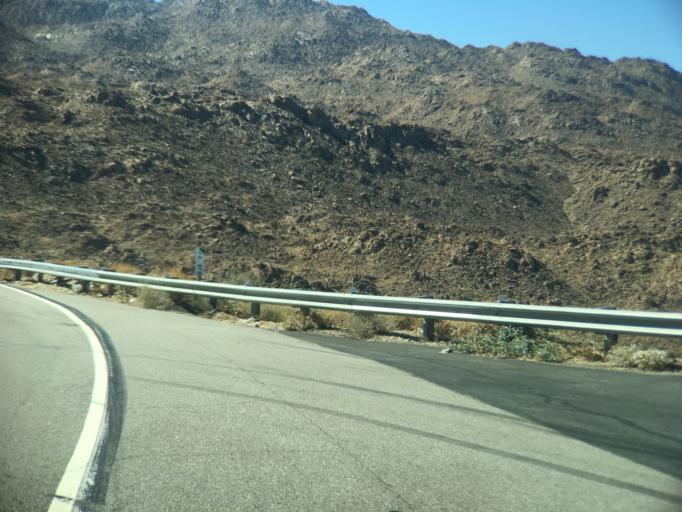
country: US
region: California
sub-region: Riverside County
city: Palm Desert
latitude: 33.6491
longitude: -116.4010
